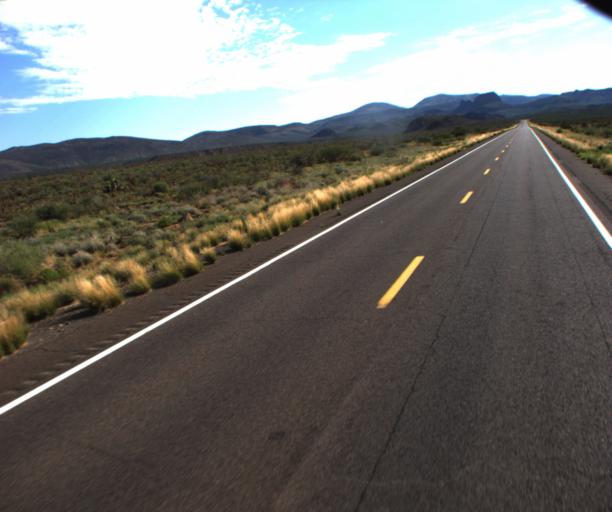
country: US
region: Arizona
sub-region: Greenlee County
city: Morenci
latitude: 32.8384
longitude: -109.4306
